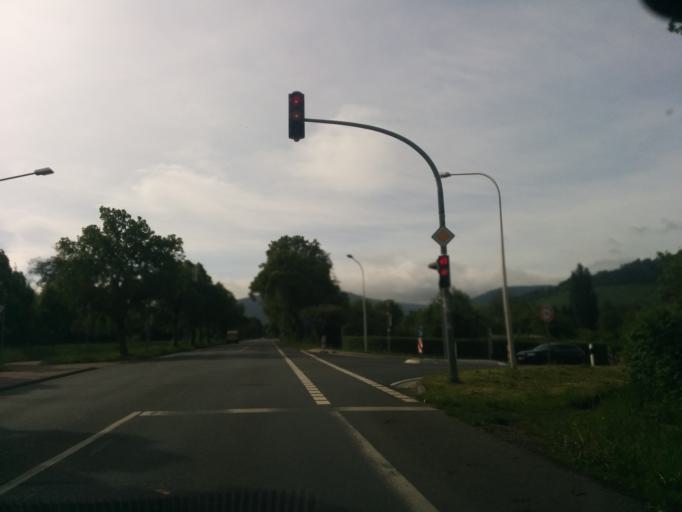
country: DE
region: Lower Saxony
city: Goslar
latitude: 51.9221
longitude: 10.4136
